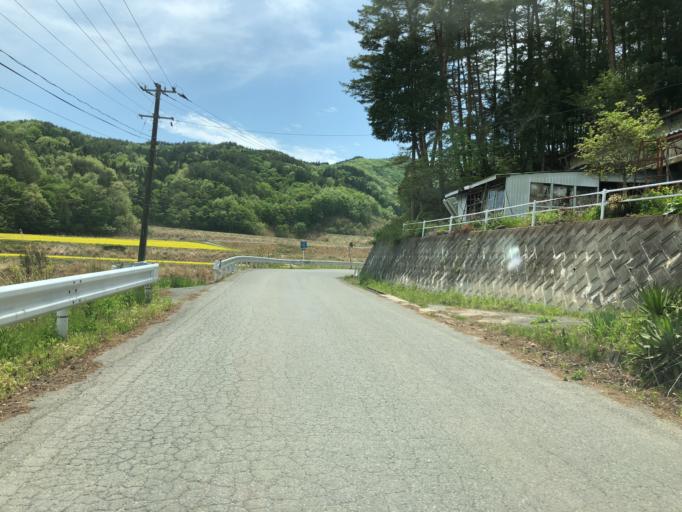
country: JP
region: Fukushima
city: Yanagawamachi-saiwaicho
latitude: 37.7191
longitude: 140.7160
